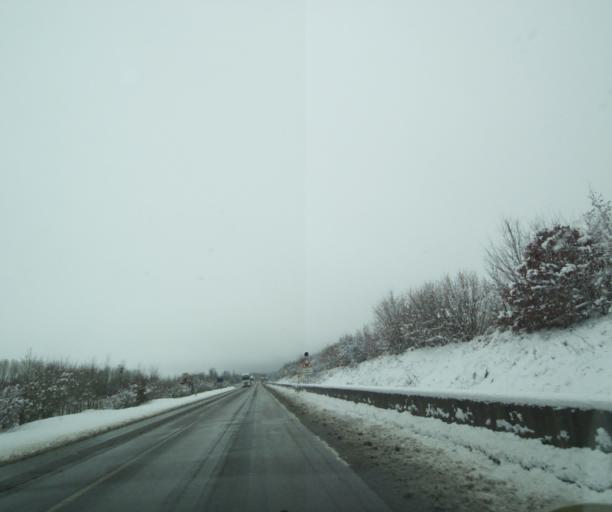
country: FR
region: Champagne-Ardenne
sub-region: Departement de la Haute-Marne
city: Saint-Dizier
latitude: 48.5825
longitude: 4.8875
